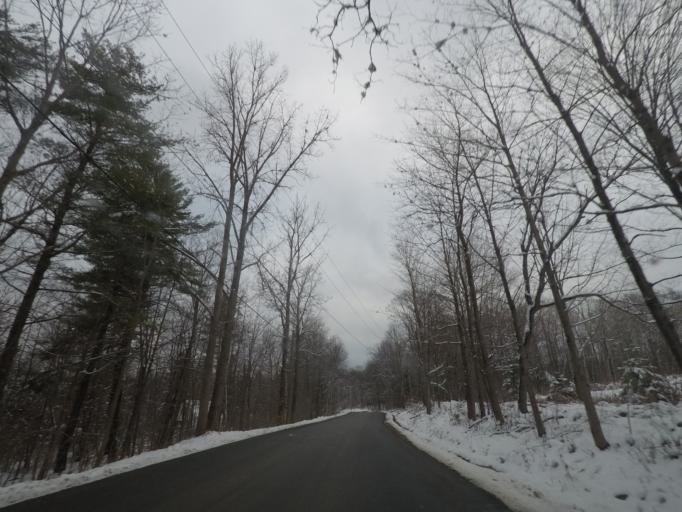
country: US
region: New York
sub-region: Rensselaer County
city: Averill Park
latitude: 42.6584
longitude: -73.5328
